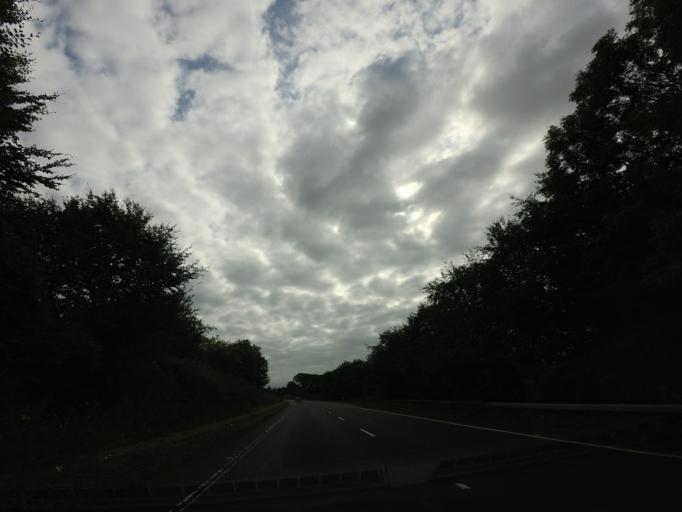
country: GB
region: Scotland
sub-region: Dumfries and Galloway
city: Annan
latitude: 54.9954
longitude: -3.2788
